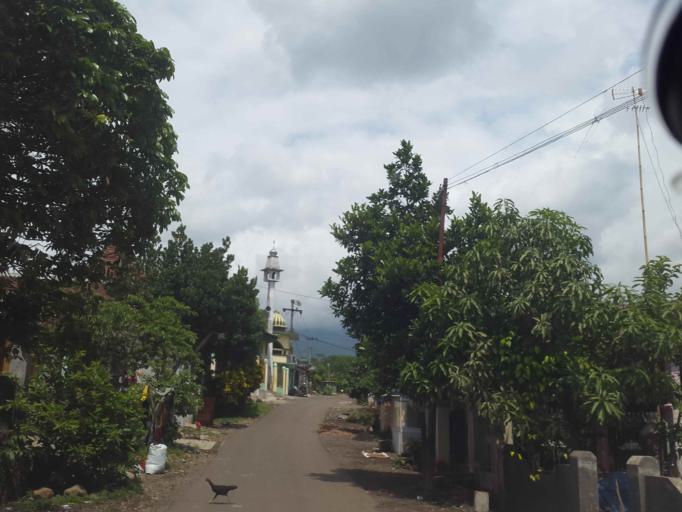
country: ID
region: East Java
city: Singosari
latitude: -7.8638
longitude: 112.6463
